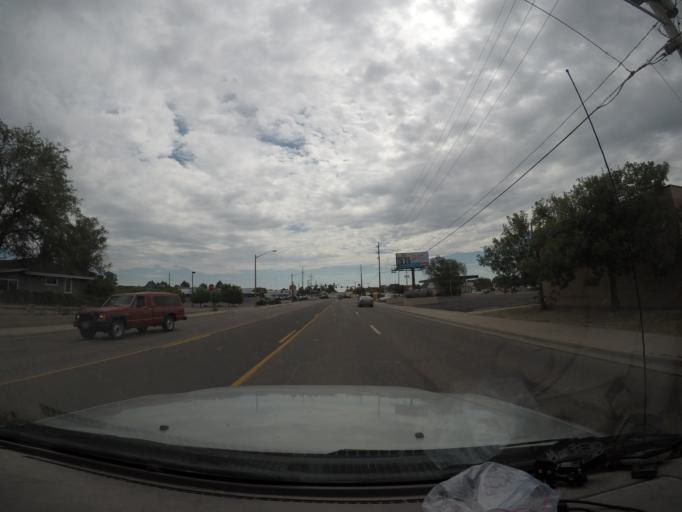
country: US
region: Wyoming
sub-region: Laramie County
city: Fox Farm-College
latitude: 41.1456
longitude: -104.7703
